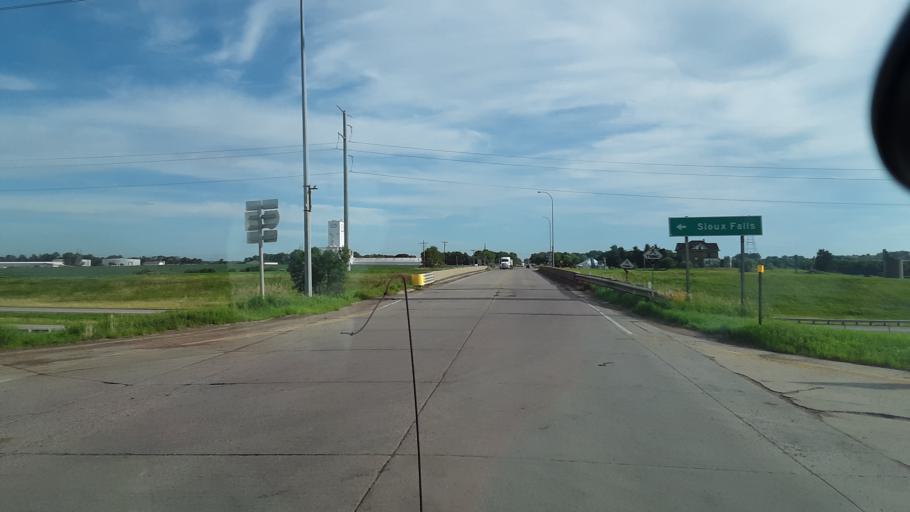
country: US
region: South Dakota
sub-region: Minnehaha County
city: Brandon
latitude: 43.6077
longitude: -96.5722
